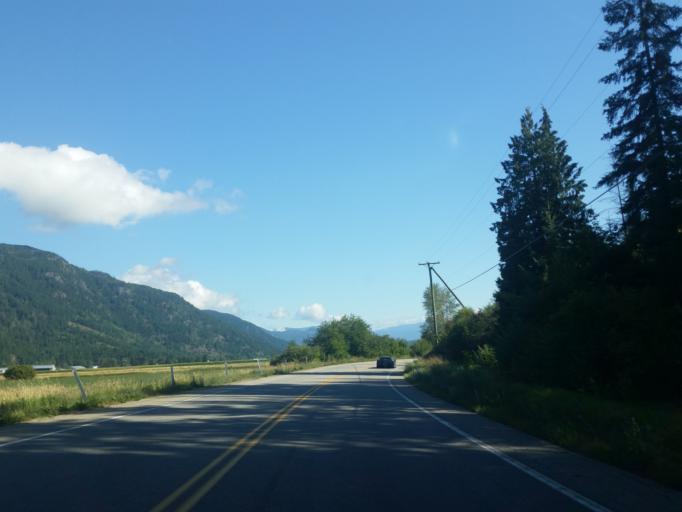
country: CA
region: British Columbia
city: Enderby
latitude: 50.6619
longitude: -119.0742
